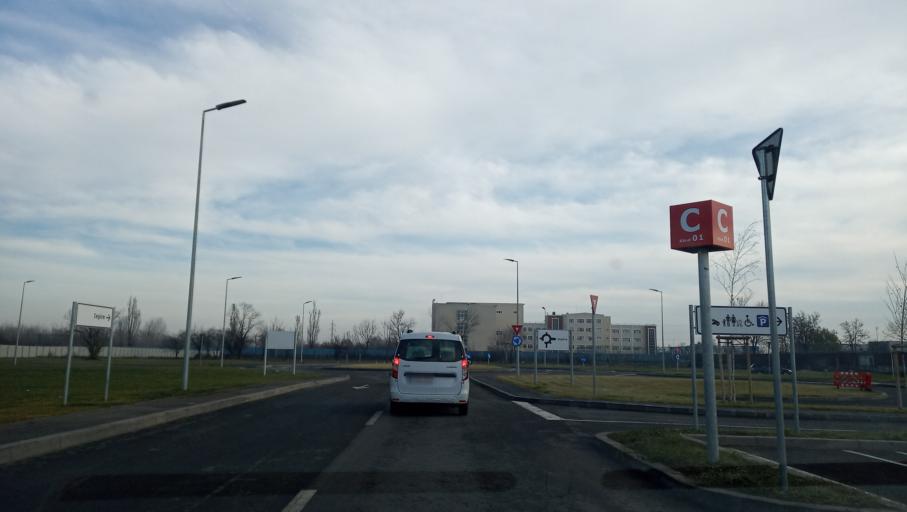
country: RO
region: Ilfov
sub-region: Comuna Glina
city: Catelu
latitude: 44.4095
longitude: 26.2074
